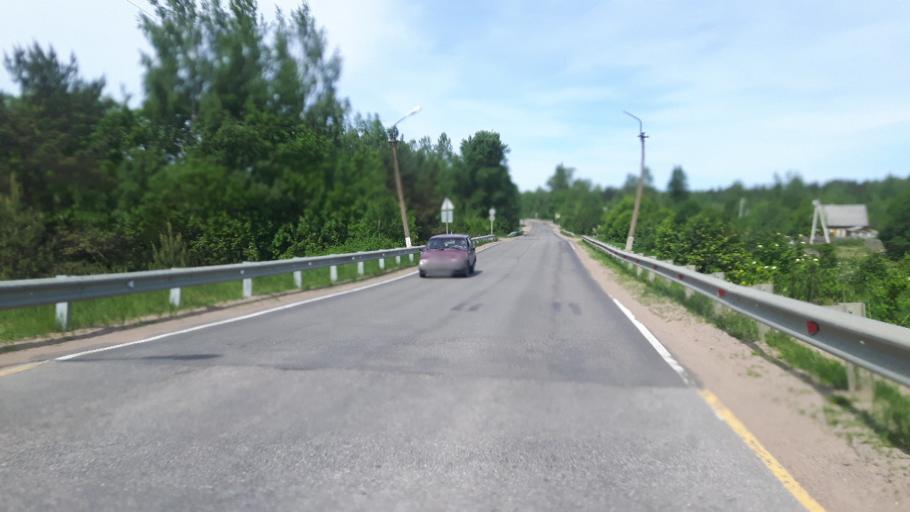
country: RU
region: Leningrad
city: Ust'-Luga
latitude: 59.6538
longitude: 28.2569
